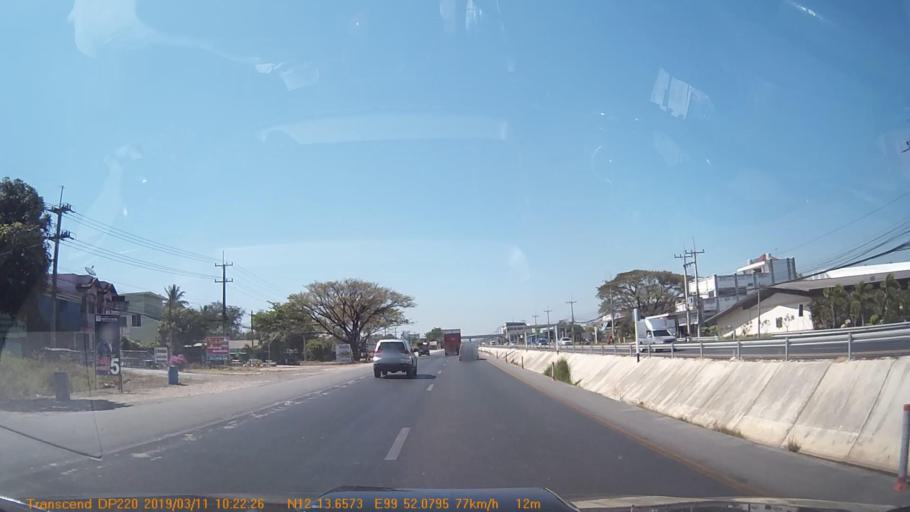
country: TH
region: Prachuap Khiri Khan
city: Sam Roi Yot
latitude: 12.2274
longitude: 99.8679
